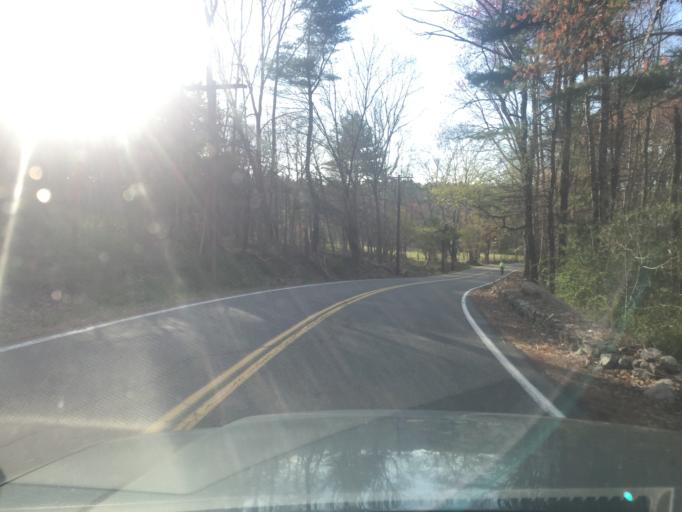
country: US
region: Massachusetts
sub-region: Middlesex County
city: Sherborn
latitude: 42.2310
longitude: -71.3284
